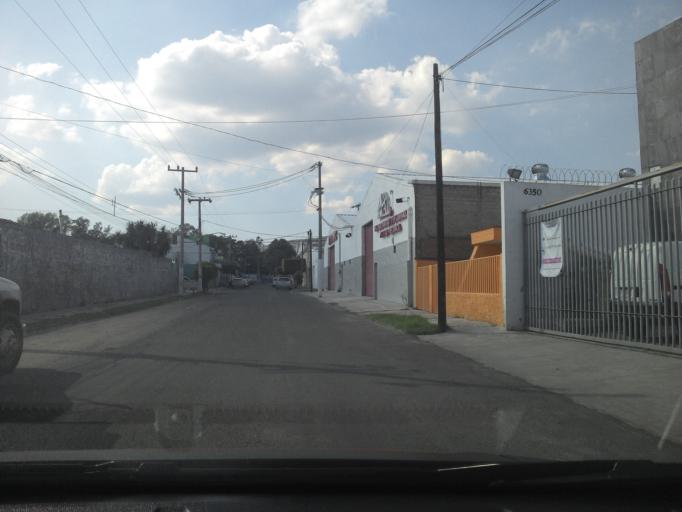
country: MX
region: Jalisco
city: Guadalajara
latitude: 20.6462
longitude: -103.4370
